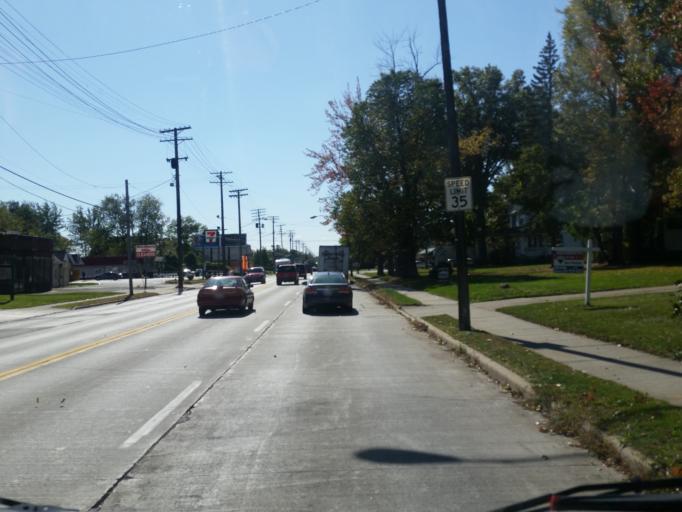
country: US
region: Ohio
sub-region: Cuyahoga County
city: Rocky River
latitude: 41.4453
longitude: -81.8183
